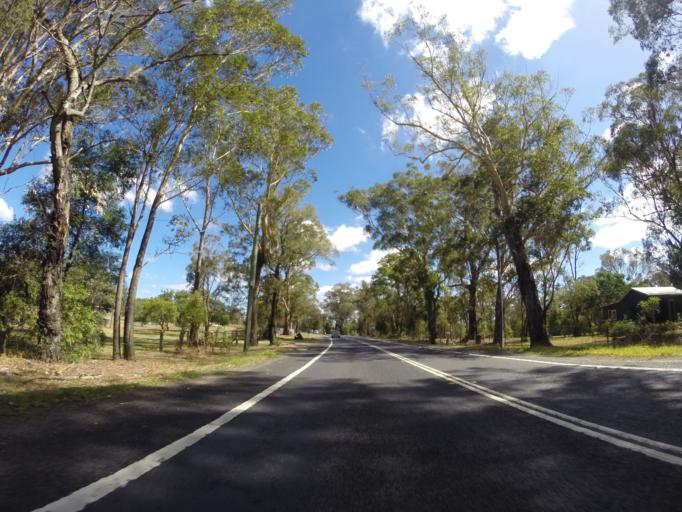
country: AU
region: New South Wales
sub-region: Campbelltown Municipality
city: Glen Alpine
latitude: -34.1594
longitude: 150.7901
